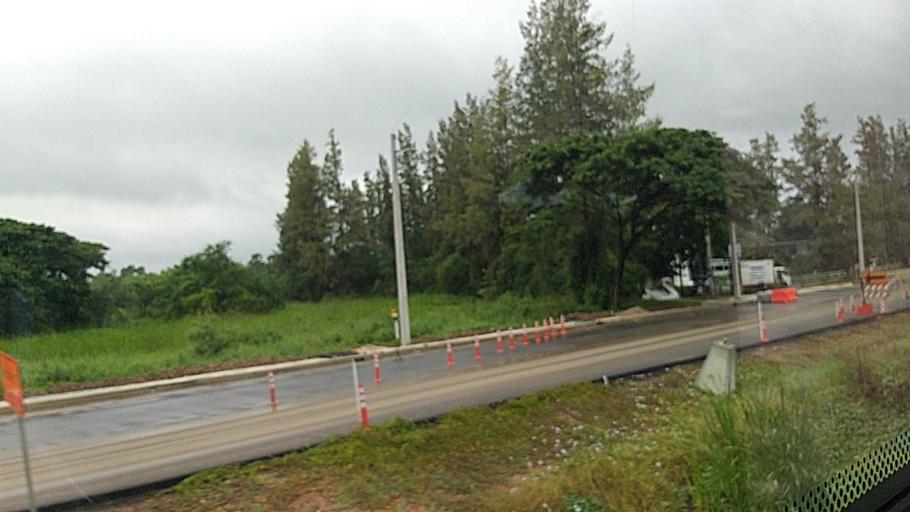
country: TH
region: Nakhon Ratchasima
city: Nakhon Ratchasima
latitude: 14.9931
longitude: 102.0639
